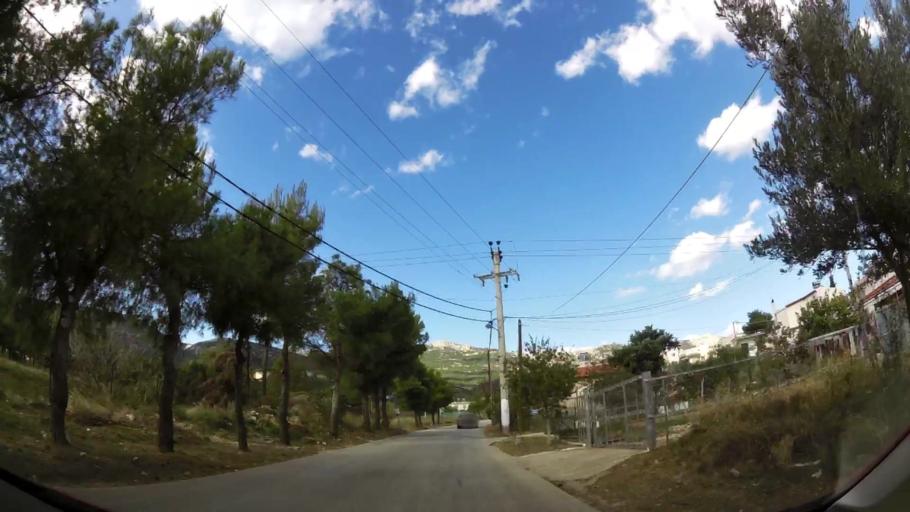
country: GR
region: Attica
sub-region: Nomarchia Anatolikis Attikis
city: Acharnes
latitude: 38.1114
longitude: 23.7315
